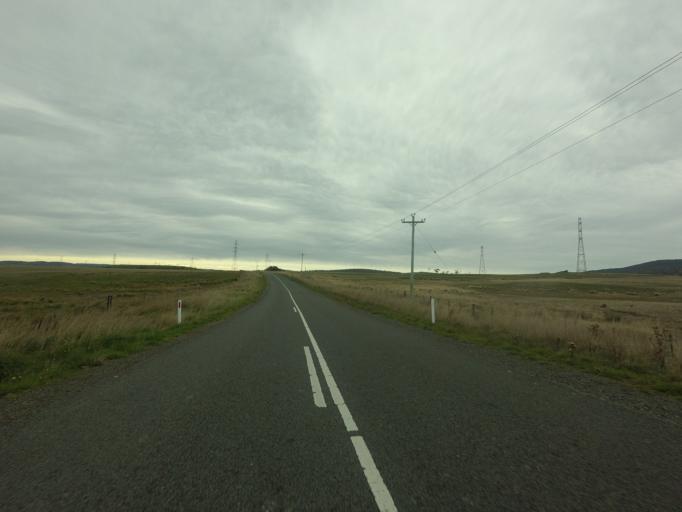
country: AU
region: Tasmania
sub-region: Derwent Valley
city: New Norfolk
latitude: -42.4219
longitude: 147.0009
